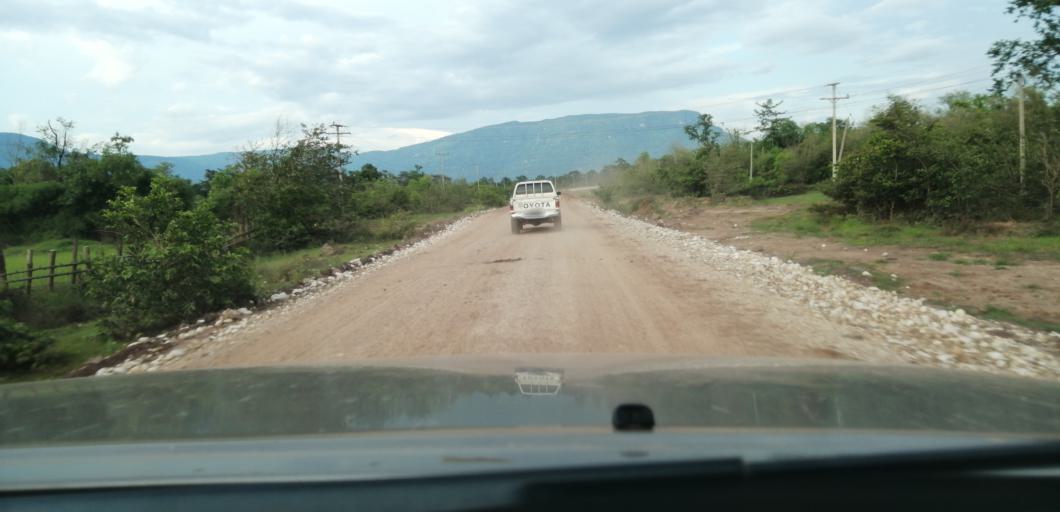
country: LA
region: Attapu
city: Attapu
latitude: 14.7096
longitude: 106.4837
